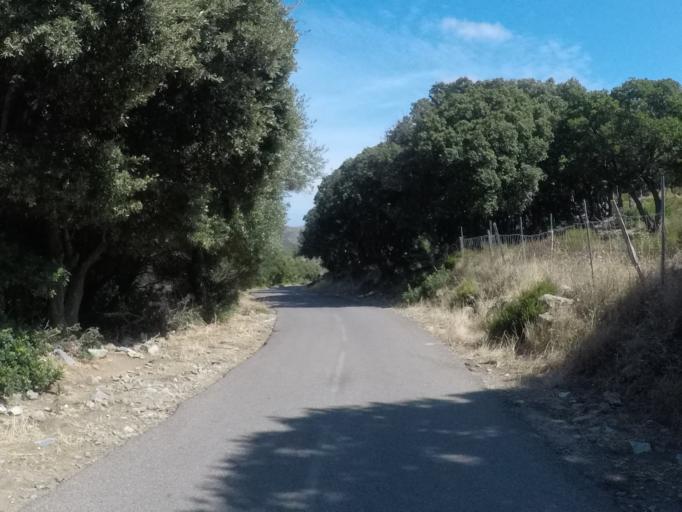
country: FR
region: Corsica
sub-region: Departement de la Haute-Corse
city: Brando
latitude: 42.9874
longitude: 9.4005
